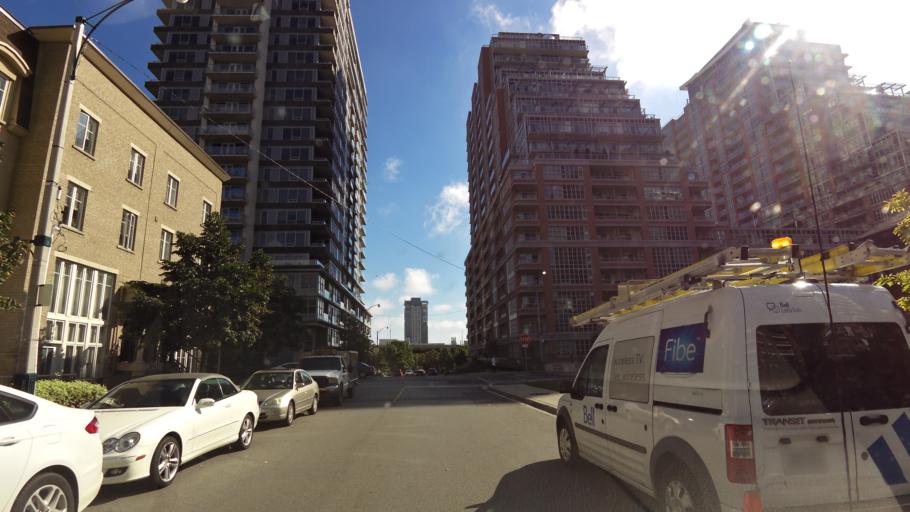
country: CA
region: Ontario
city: Toronto
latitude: 43.6391
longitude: -79.4141
